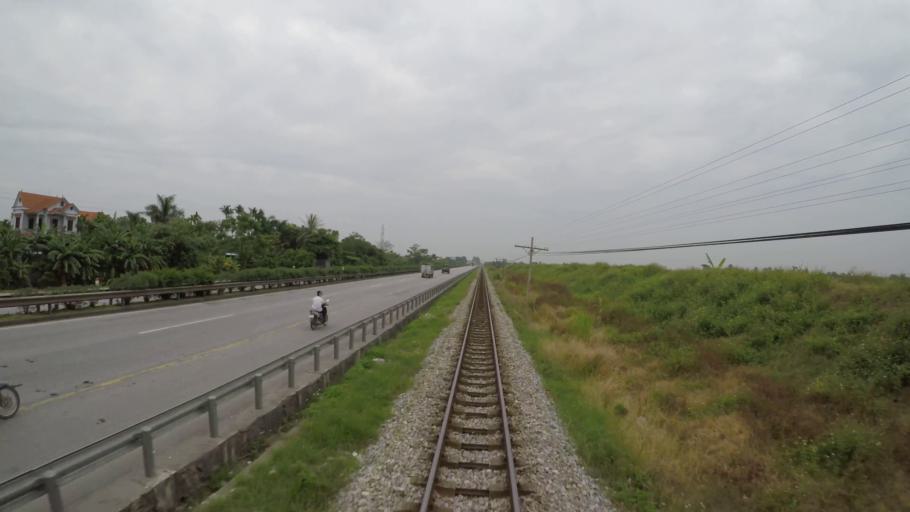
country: VN
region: Hai Duong
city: Nam Sach
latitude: 20.9765
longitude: 106.4032
